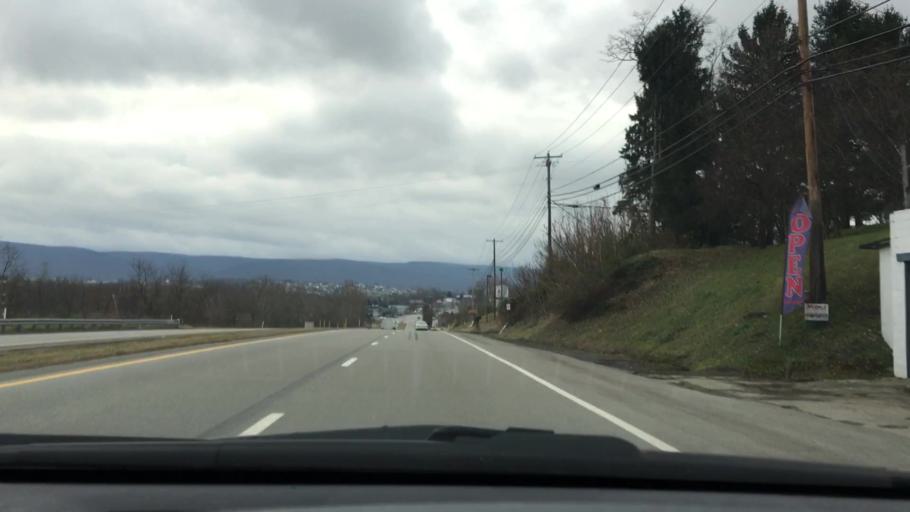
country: US
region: Pennsylvania
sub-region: Fayette County
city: Oliver
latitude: 39.9332
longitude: -79.7289
